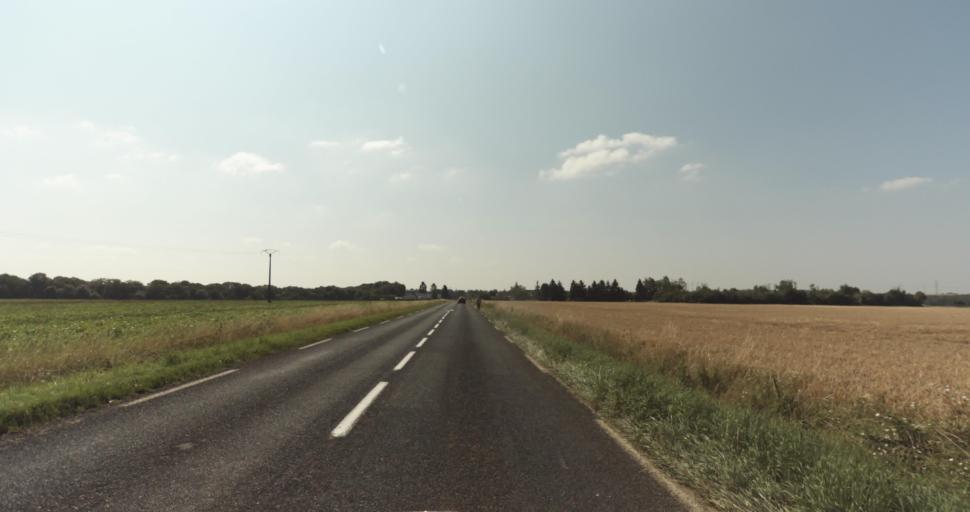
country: FR
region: Lorraine
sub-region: Departement de Meurthe-et-Moselle
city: Briey
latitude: 49.2534
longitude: 5.9237
